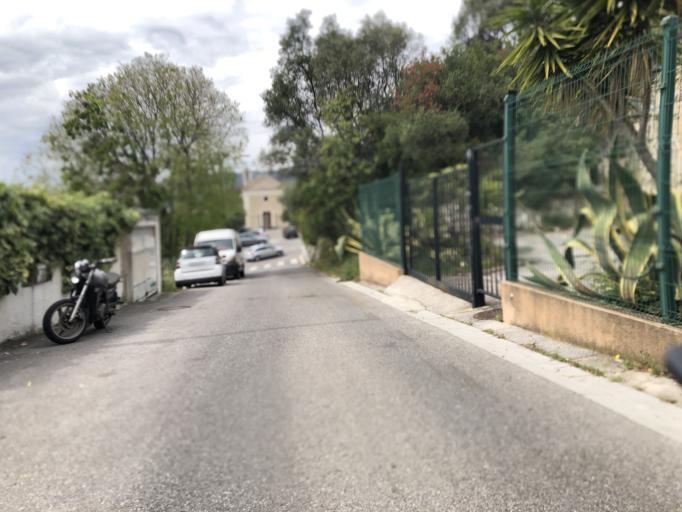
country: FR
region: Provence-Alpes-Cote d'Azur
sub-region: Departement des Alpes-Maritimes
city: Villefranche-sur-Mer
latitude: 43.7197
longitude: 7.2969
